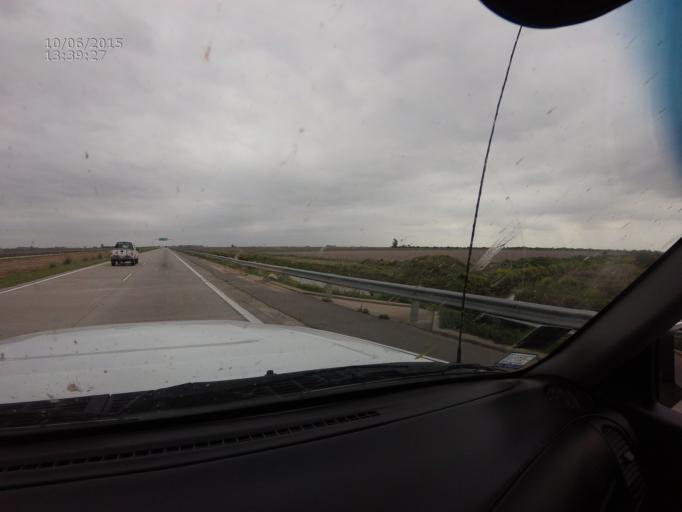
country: AR
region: Cordoba
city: Leones
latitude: -32.6001
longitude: -62.4570
